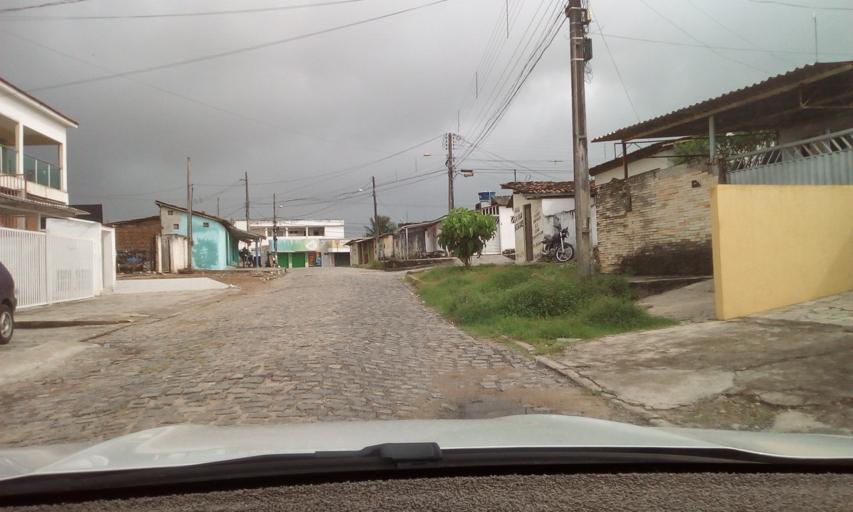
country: BR
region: Paraiba
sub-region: Bayeux
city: Bayeux
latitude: -7.1554
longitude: -34.9028
